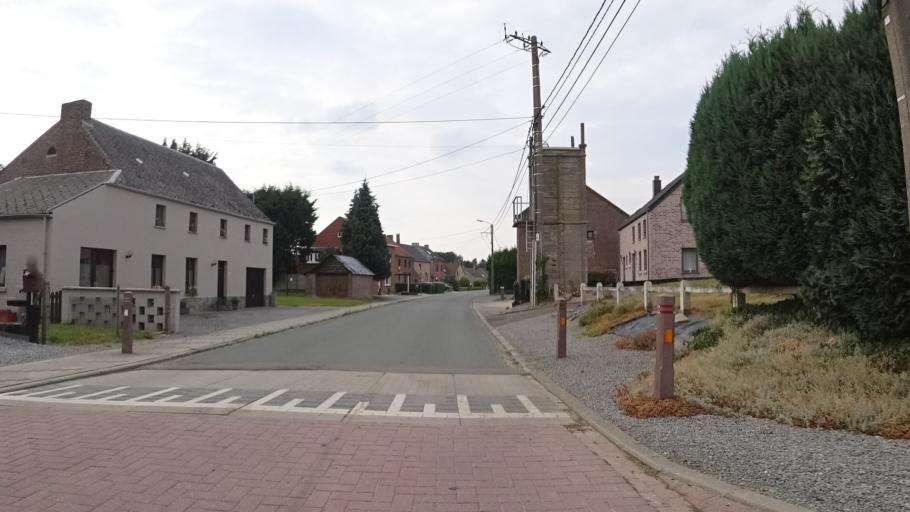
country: BE
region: Wallonia
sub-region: Province de Namur
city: Eghezee
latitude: 50.5550
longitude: 4.8602
